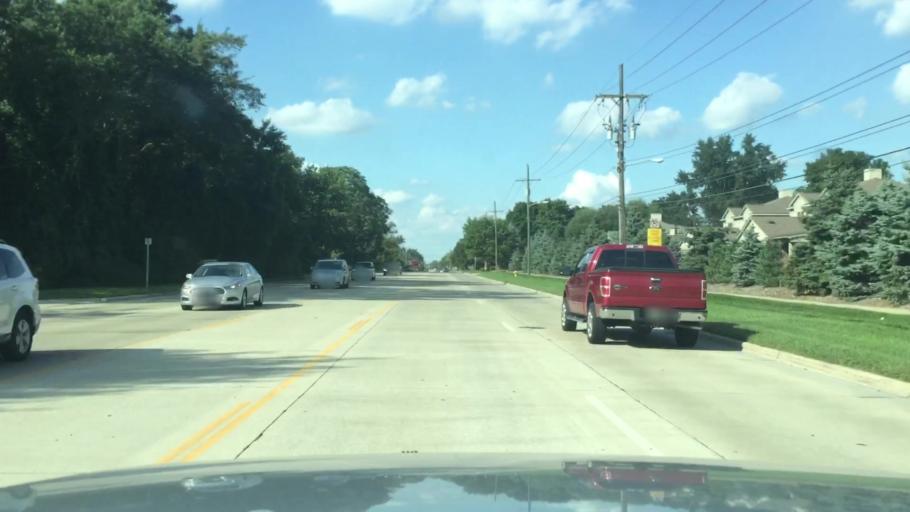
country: US
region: Michigan
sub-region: Wayne County
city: Westland
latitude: 42.3277
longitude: -83.4087
